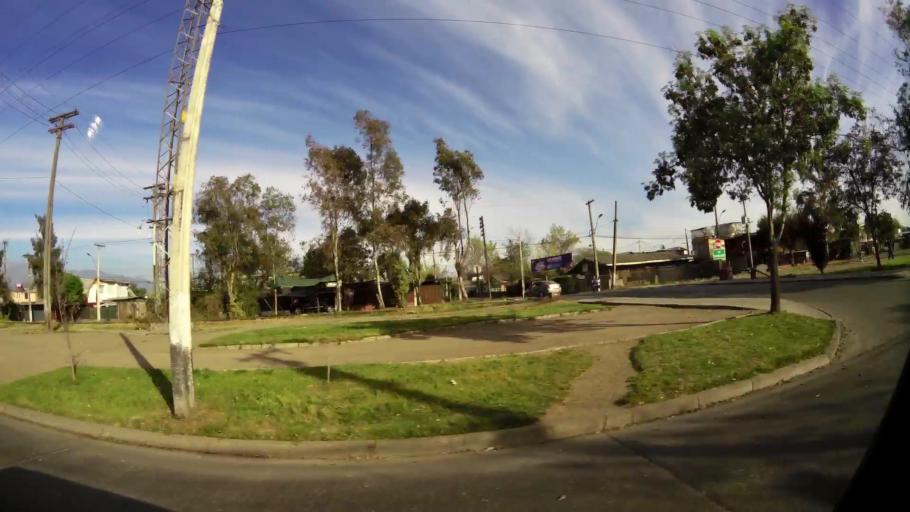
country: CL
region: Santiago Metropolitan
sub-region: Provincia de Santiago
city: Lo Prado
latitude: -33.4757
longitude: -70.6915
